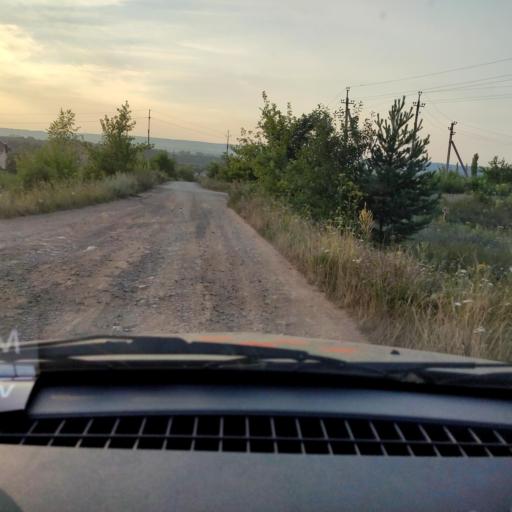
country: RU
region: Bashkortostan
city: Avdon
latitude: 54.5878
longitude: 55.6785
